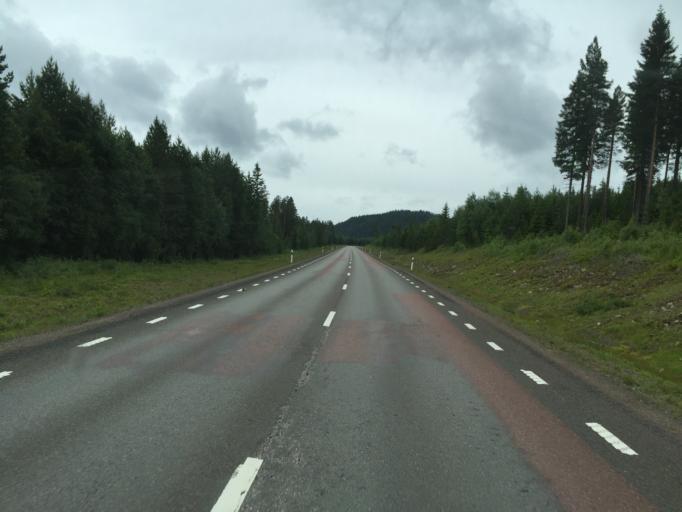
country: SE
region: Dalarna
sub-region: Malung-Saelens kommun
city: Malung
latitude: 60.6211
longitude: 13.6088
